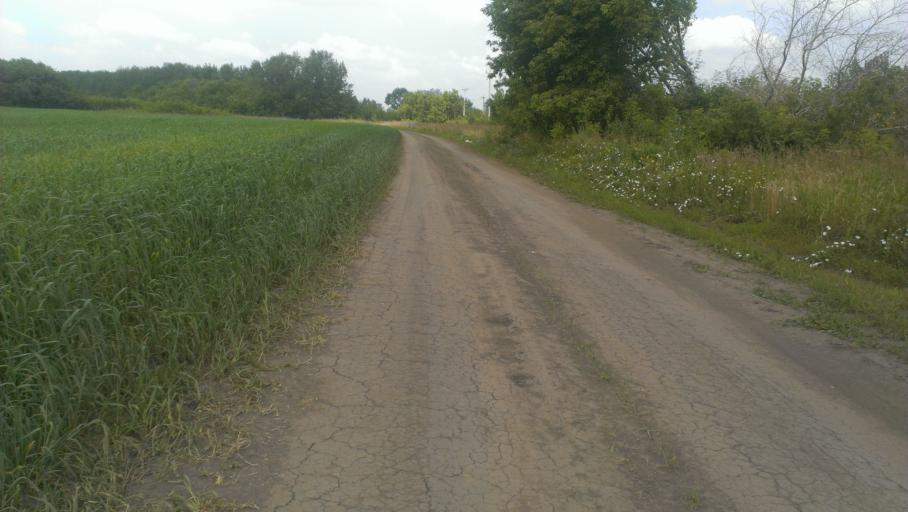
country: RU
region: Altai Krai
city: Gon'ba
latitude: 53.3831
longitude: 83.6246
